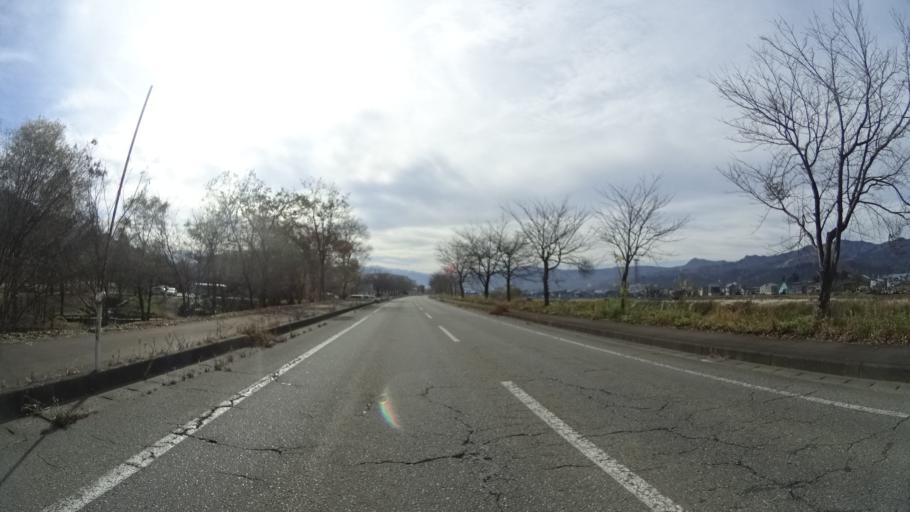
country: JP
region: Niigata
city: Muikamachi
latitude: 37.0698
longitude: 138.8871
